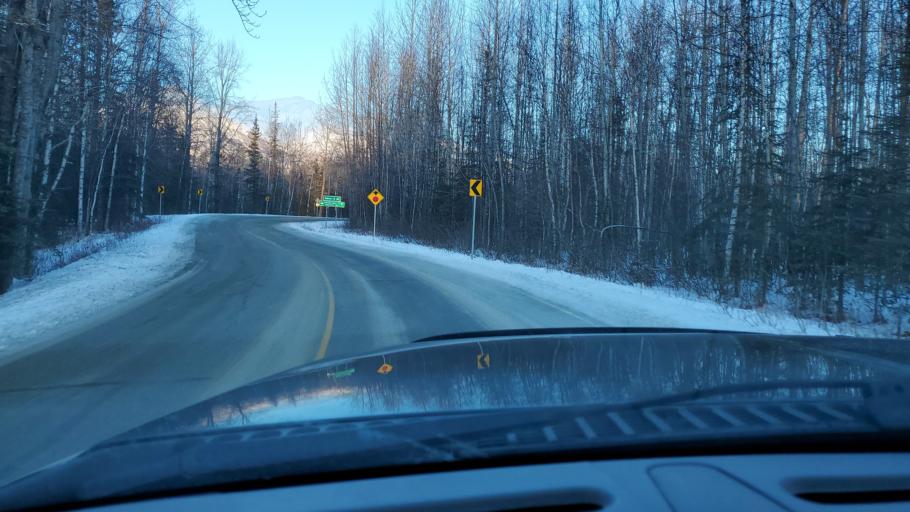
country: US
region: Alaska
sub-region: Matanuska-Susitna Borough
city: Fishhook
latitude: 61.6877
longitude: -149.2444
